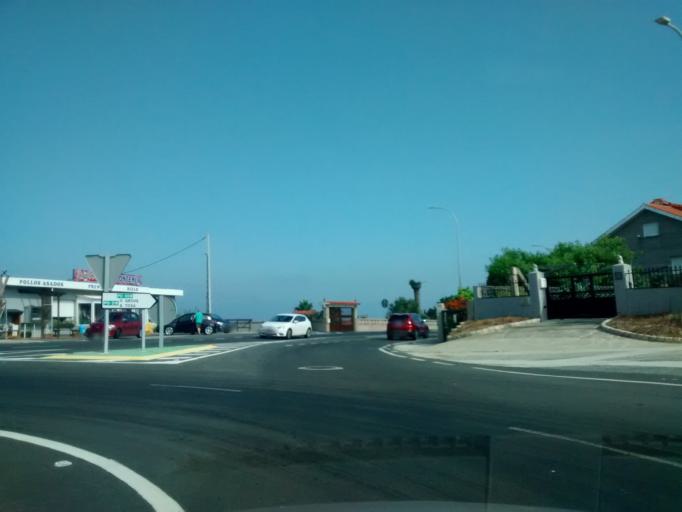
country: ES
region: Galicia
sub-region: Provincia de Pontevedra
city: Sanxenxo
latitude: 42.4221
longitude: -8.8739
